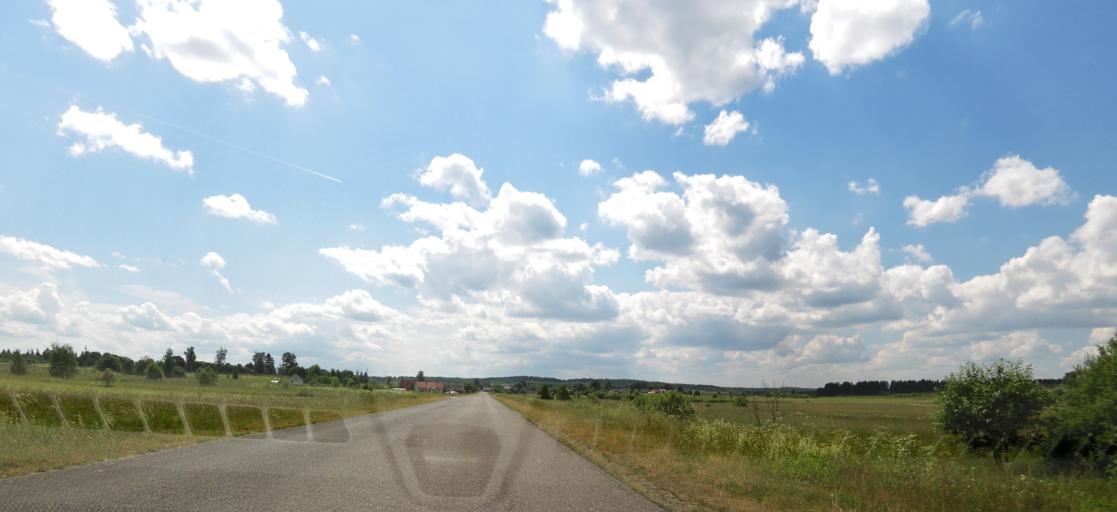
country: LT
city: Skaidiskes
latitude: 54.5489
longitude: 25.6550
